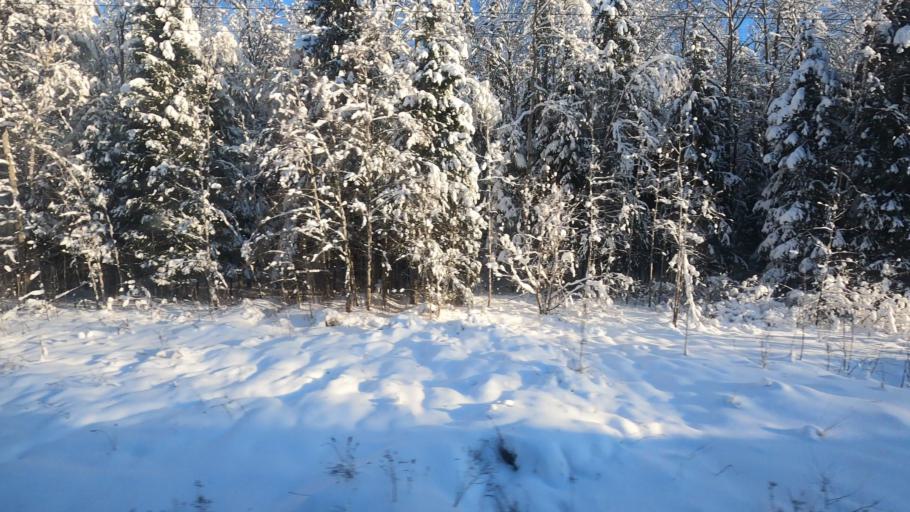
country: RU
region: Moskovskaya
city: Novo-Nikol'skoye
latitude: 56.6201
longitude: 37.5657
